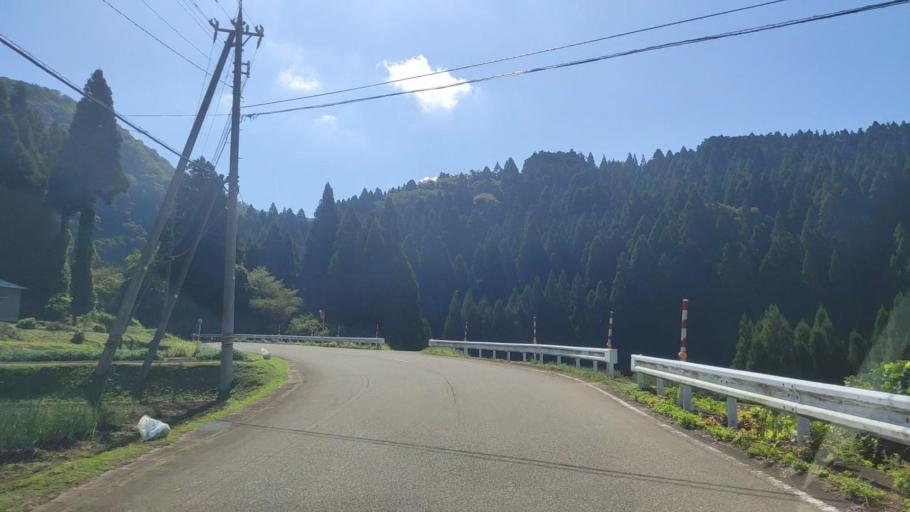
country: JP
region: Ishikawa
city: Nanao
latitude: 37.3515
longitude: 136.8670
